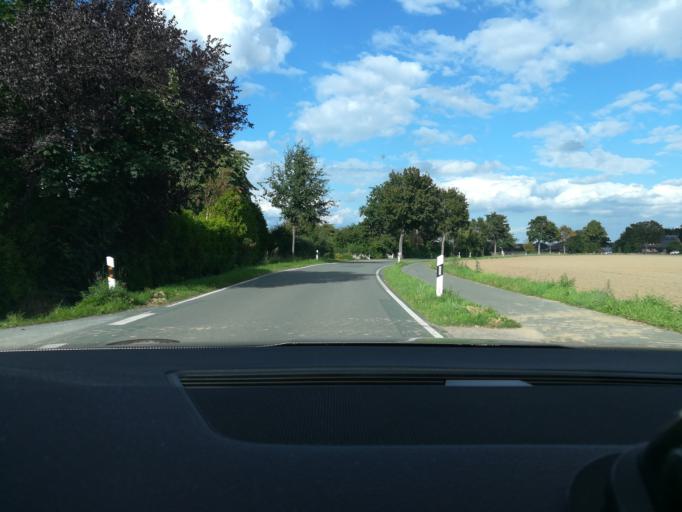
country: DE
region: North Rhine-Westphalia
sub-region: Regierungsbezirk Detmold
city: Hille
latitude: 52.3081
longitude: 8.7150
